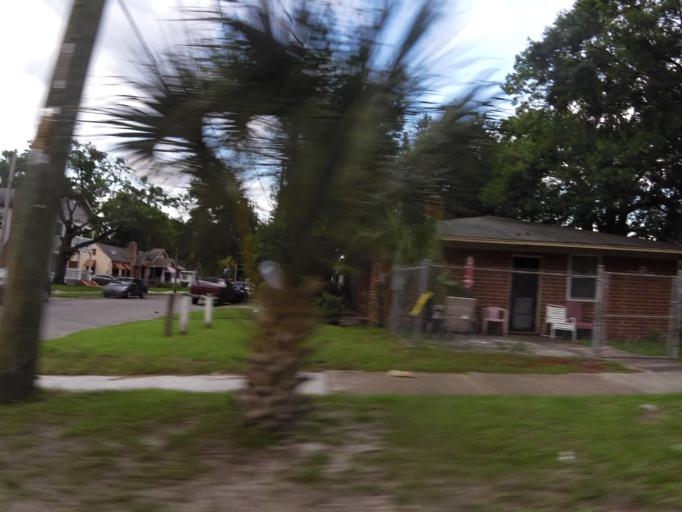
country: US
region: Florida
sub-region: Duval County
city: Jacksonville
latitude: 30.3534
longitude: -81.6612
